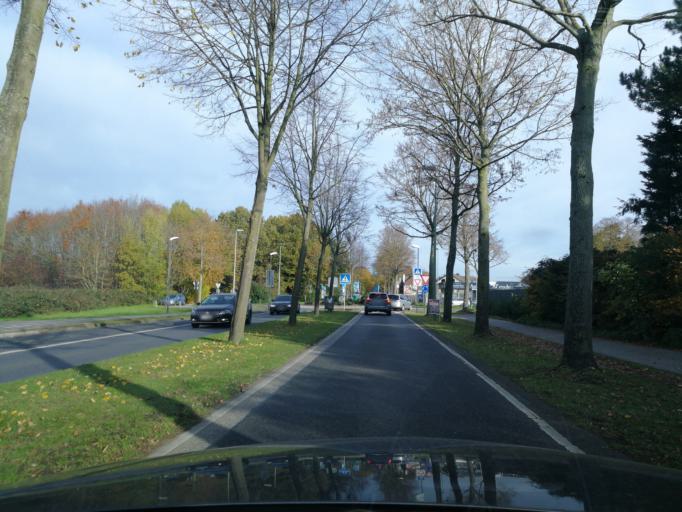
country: DE
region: North Rhine-Westphalia
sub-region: Regierungsbezirk Dusseldorf
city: Meerbusch
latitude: 51.2999
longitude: 6.6676
